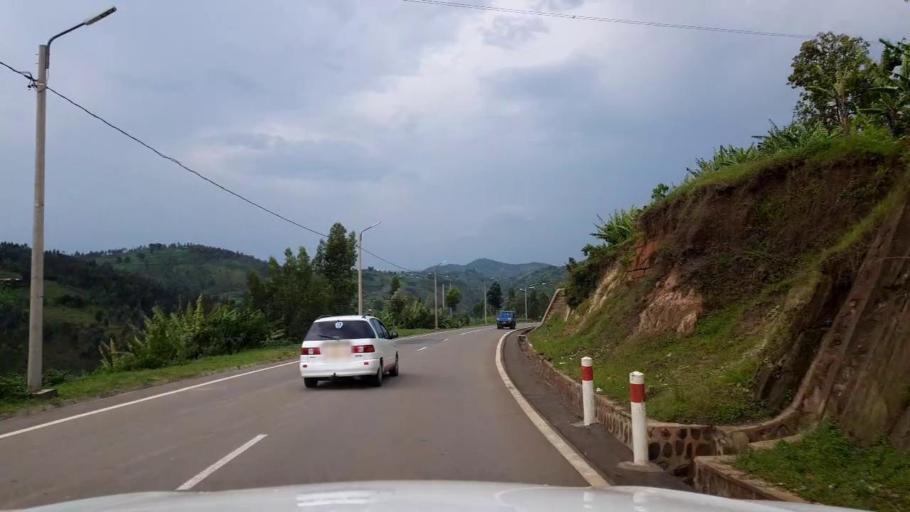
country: RW
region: Western Province
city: Kibuye
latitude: -2.0383
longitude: 29.4022
